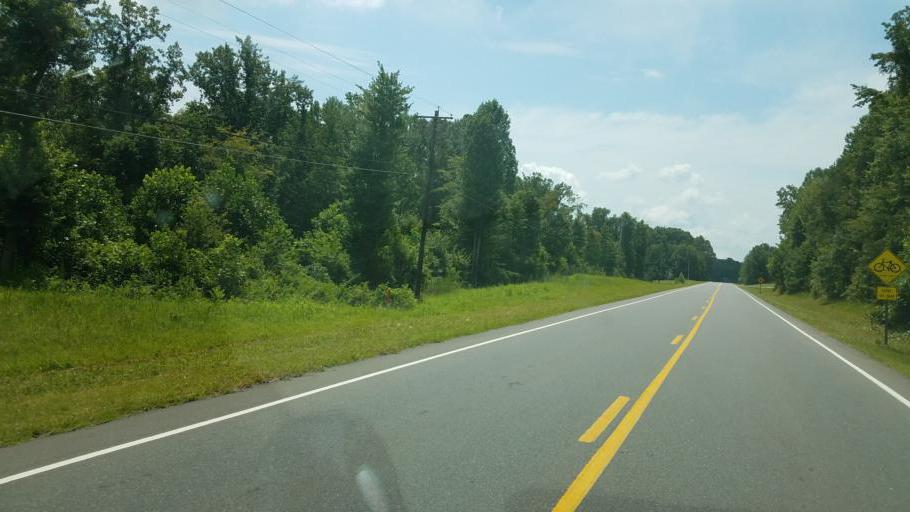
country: US
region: North Carolina
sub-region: Cleveland County
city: Kings Mountain
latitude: 35.2007
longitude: -81.3412
